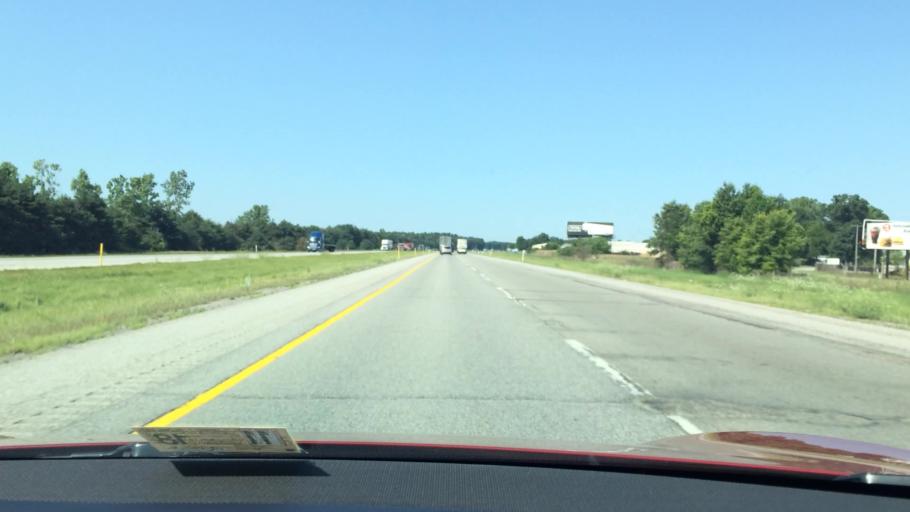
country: US
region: Indiana
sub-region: Elkhart County
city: Middlebury
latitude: 41.7403
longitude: -85.7327
